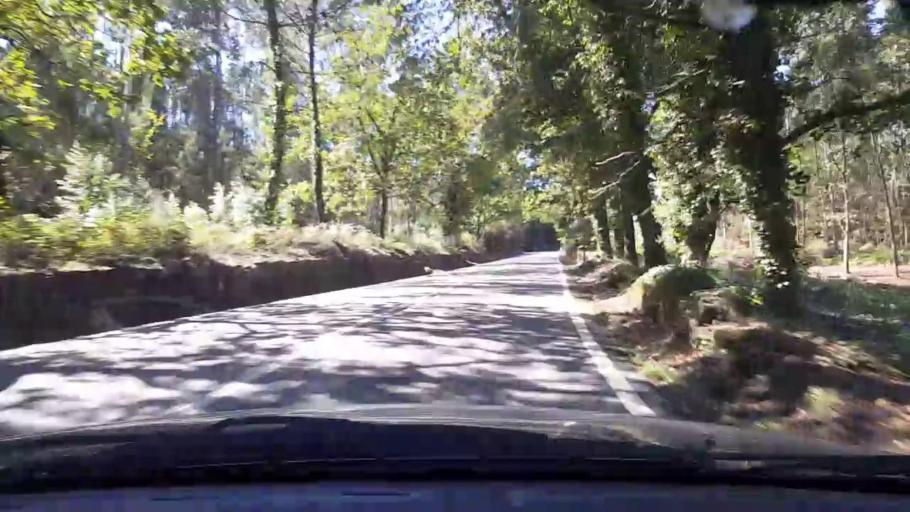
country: PT
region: Braga
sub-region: Vila Nova de Famalicao
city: Ribeirao
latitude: 41.3383
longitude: -8.6278
